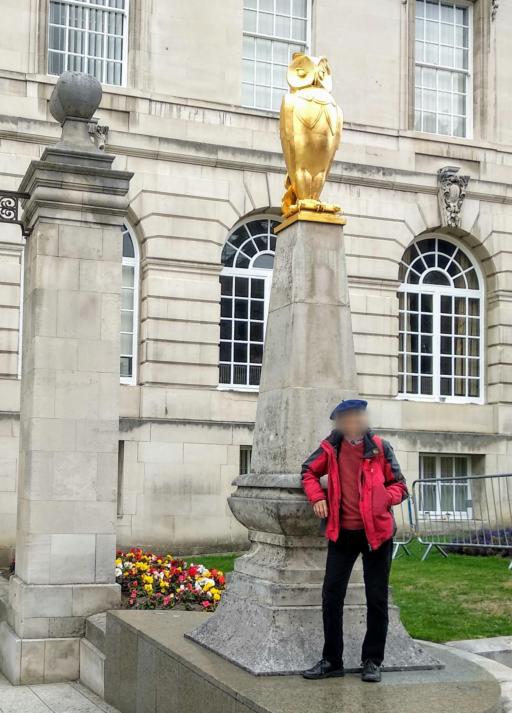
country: GB
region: England
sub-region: City and Borough of Leeds
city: Leeds
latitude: 53.8023
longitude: -1.5479
